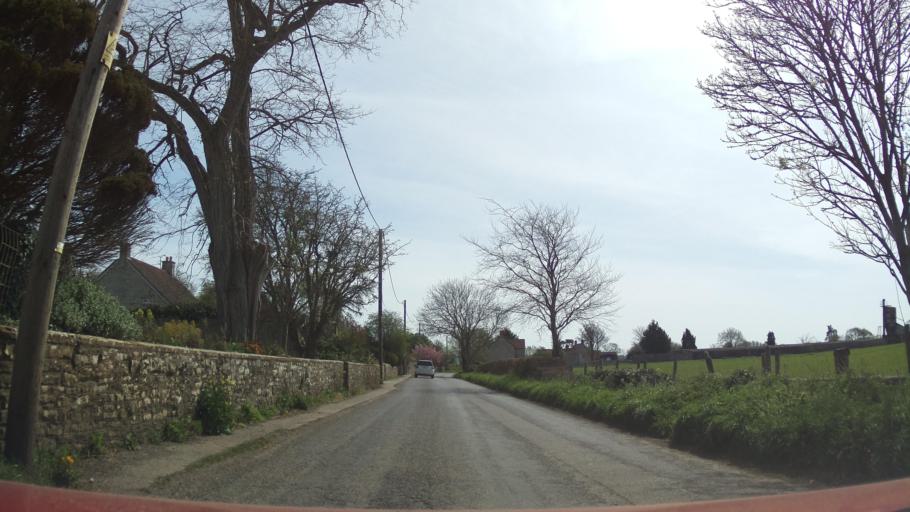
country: GB
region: England
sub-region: Somerset
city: Ilchester
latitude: 51.0151
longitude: -2.6259
